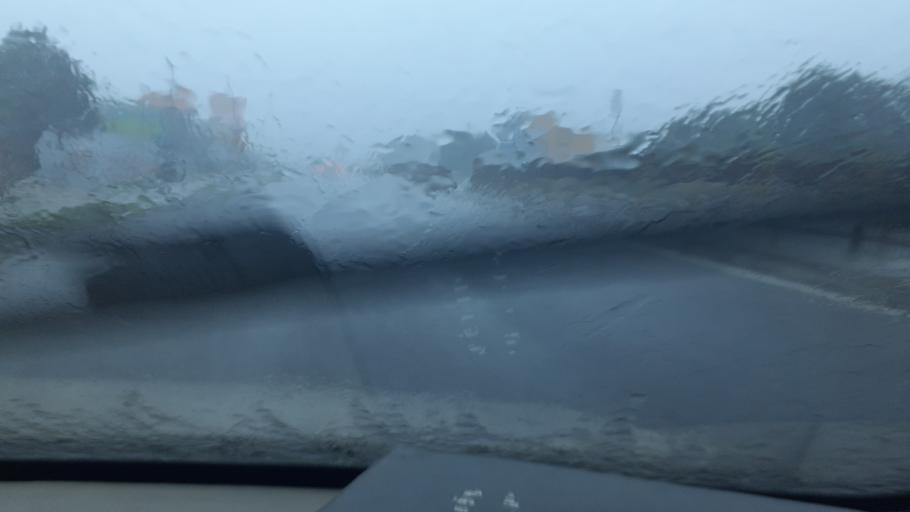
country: IN
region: Tamil Nadu
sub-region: Virudhunagar
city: Tiruttangal
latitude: 9.4629
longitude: 77.9333
